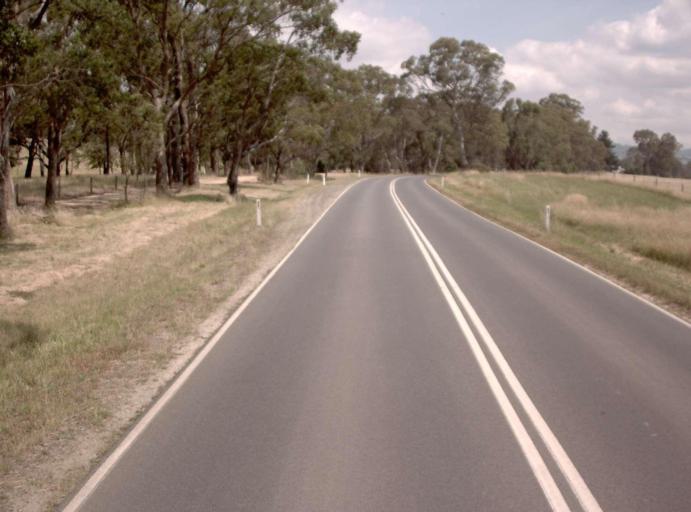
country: AU
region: Victoria
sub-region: Latrobe
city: Traralgon
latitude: -38.2663
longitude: 146.5462
